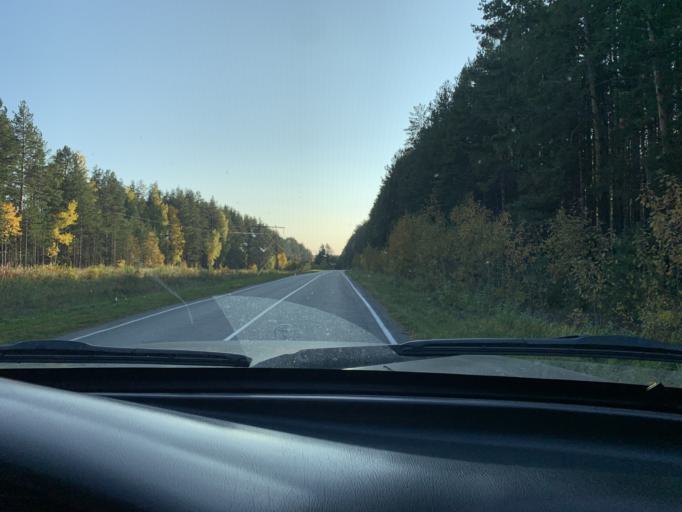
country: RU
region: Sverdlovsk
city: Verkhneye Dubrovo
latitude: 56.8662
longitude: 61.0916
